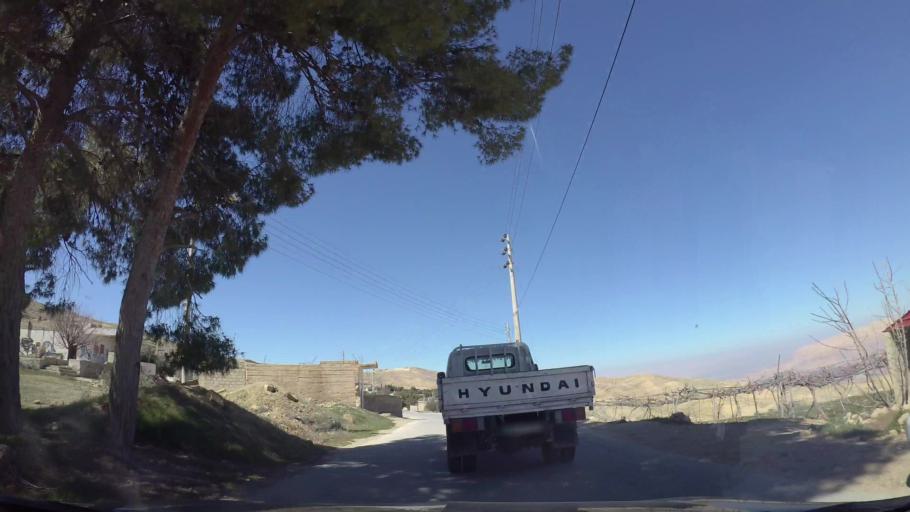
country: JO
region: Tafielah
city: At Tafilah
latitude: 30.8392
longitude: 35.5724
